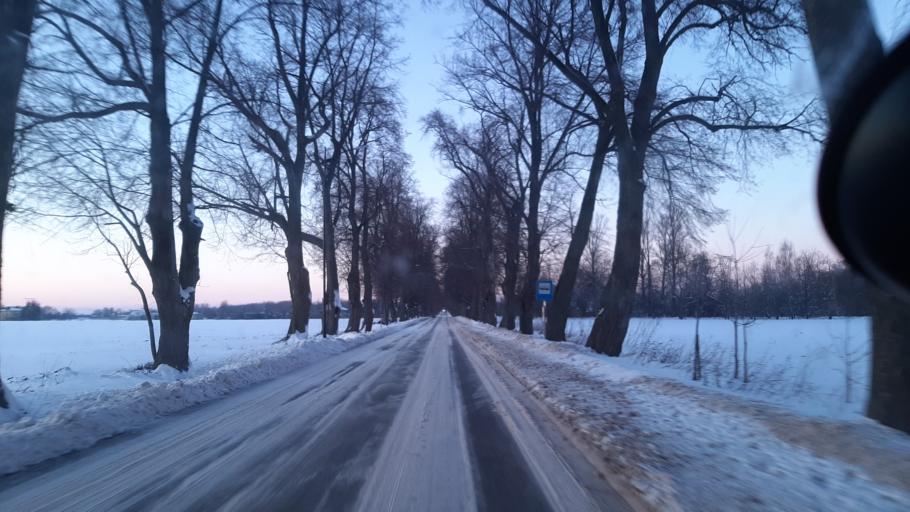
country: PL
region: Lublin Voivodeship
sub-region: Powiat lubelski
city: Lublin
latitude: 51.3261
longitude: 22.5598
